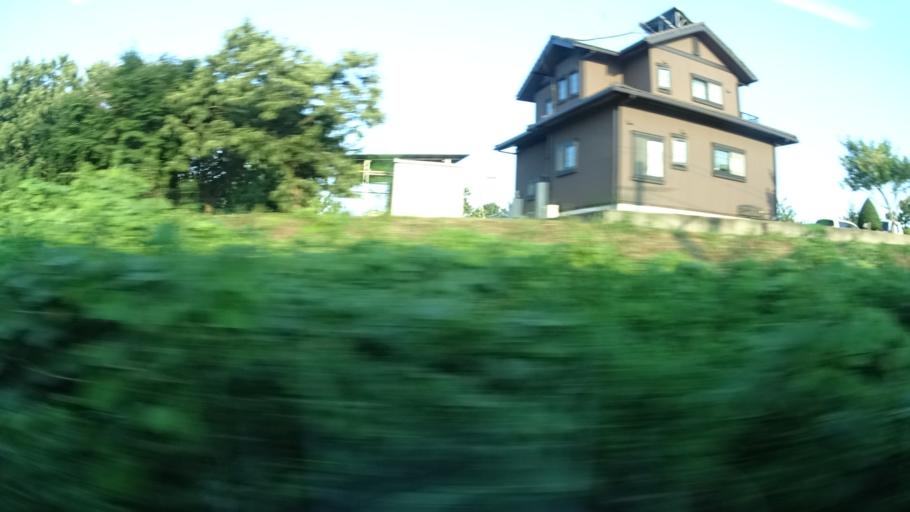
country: JP
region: Ibaraki
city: Tomobe
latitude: 36.3016
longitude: 140.2809
